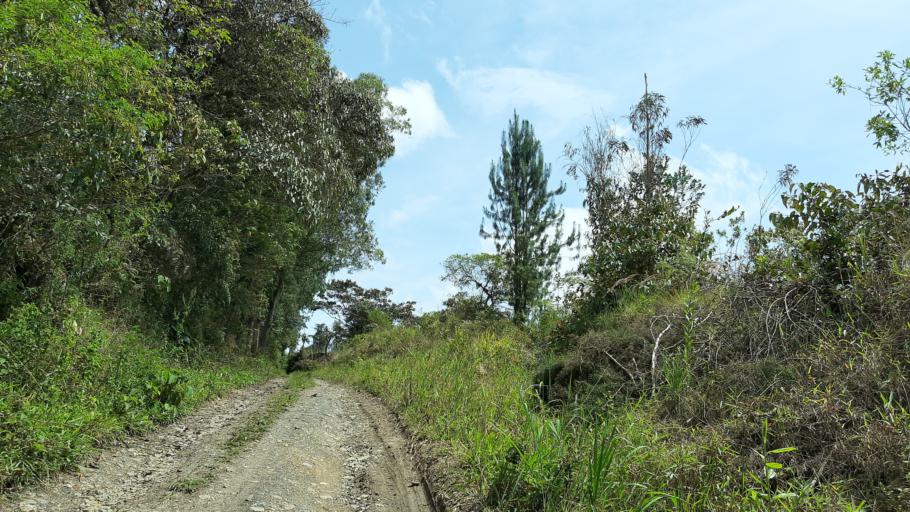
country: CO
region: Boyaca
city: Garagoa
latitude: 5.0553
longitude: -73.3541
